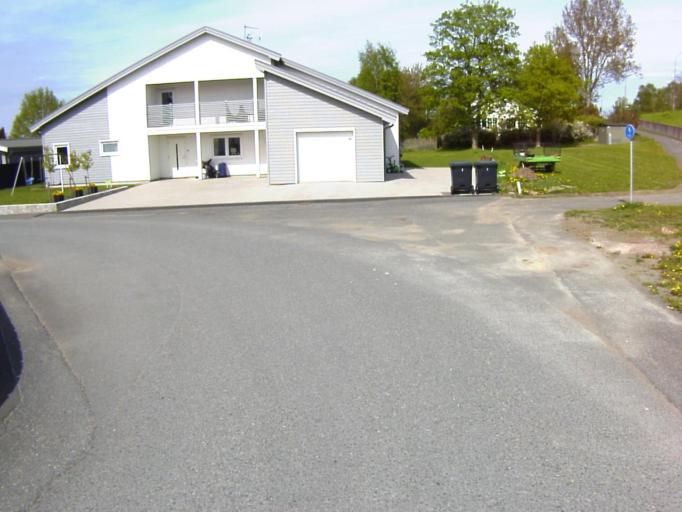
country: SE
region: Skane
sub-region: Kristianstads Kommun
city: Fjalkinge
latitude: 56.0916
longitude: 14.2379
